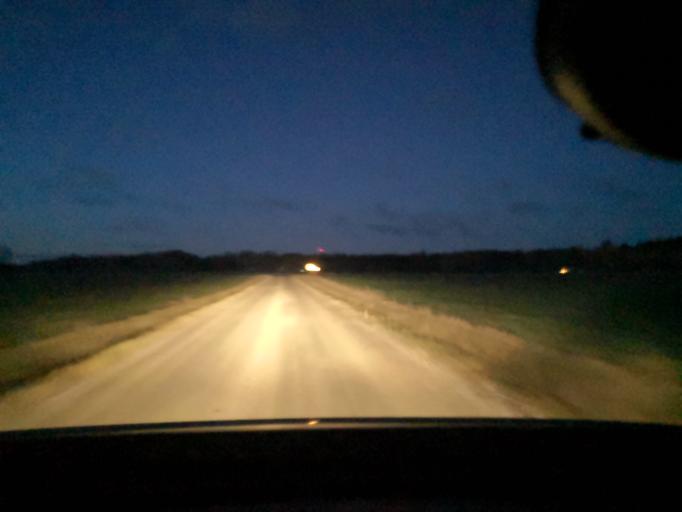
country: SE
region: Uppsala
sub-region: Heby Kommun
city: Heby
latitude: 59.9273
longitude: 16.7550
